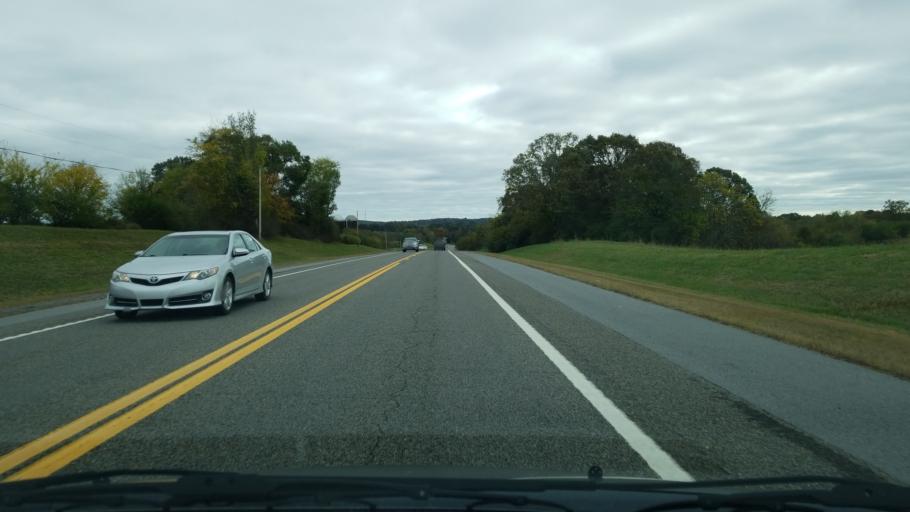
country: US
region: Tennessee
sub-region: Rhea County
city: Graysville
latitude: 35.3876
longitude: -85.0050
